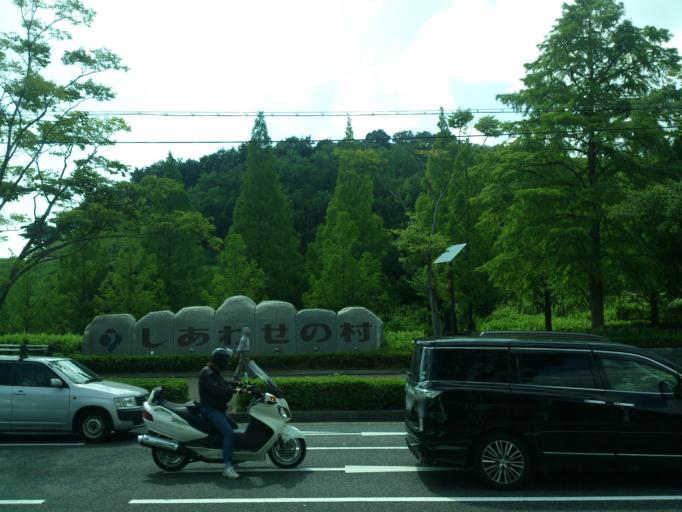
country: JP
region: Hyogo
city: Kobe
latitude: 34.7156
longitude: 135.1217
